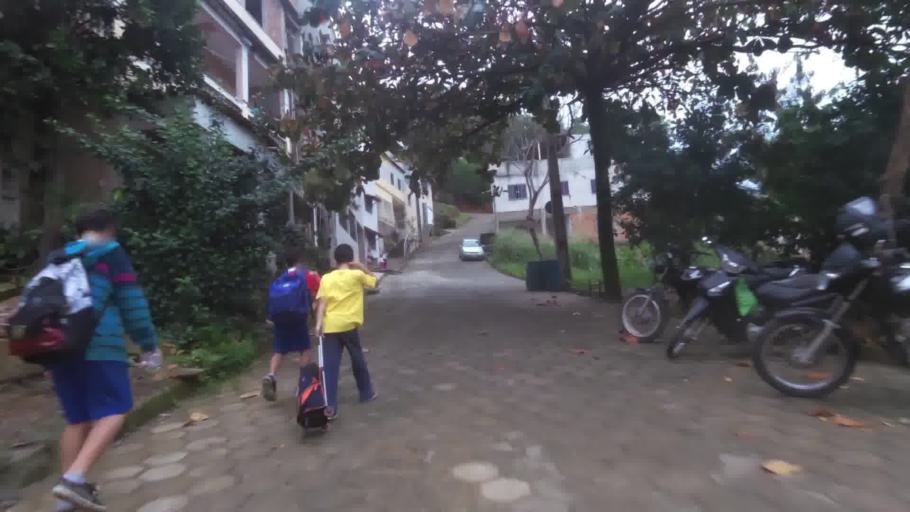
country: BR
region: Espirito Santo
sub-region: Iconha
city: Iconha
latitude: -20.7881
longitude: -40.8132
